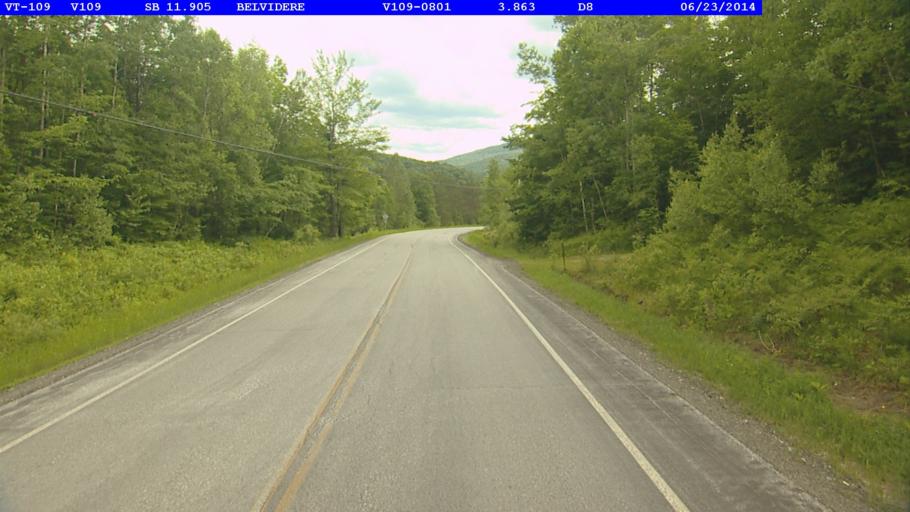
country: US
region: Vermont
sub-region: Lamoille County
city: Johnson
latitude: 44.7596
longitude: -72.6783
